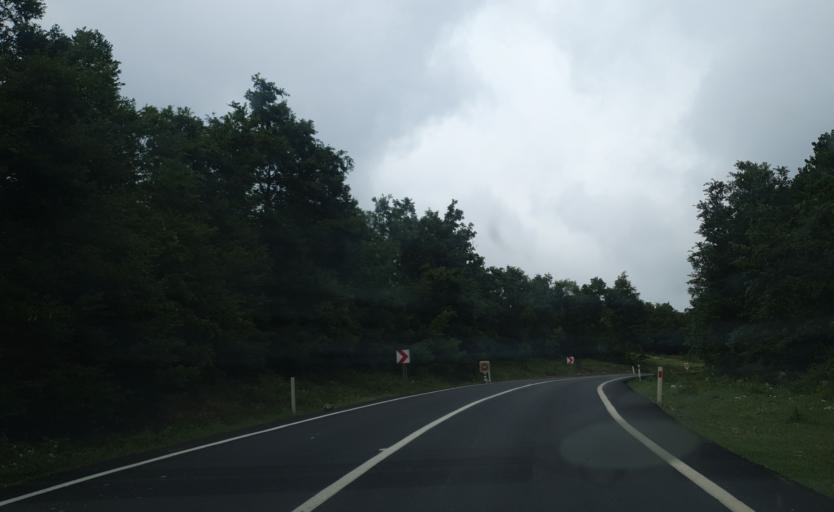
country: TR
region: Kirklareli
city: Salmydessus
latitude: 41.5875
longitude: 28.0671
